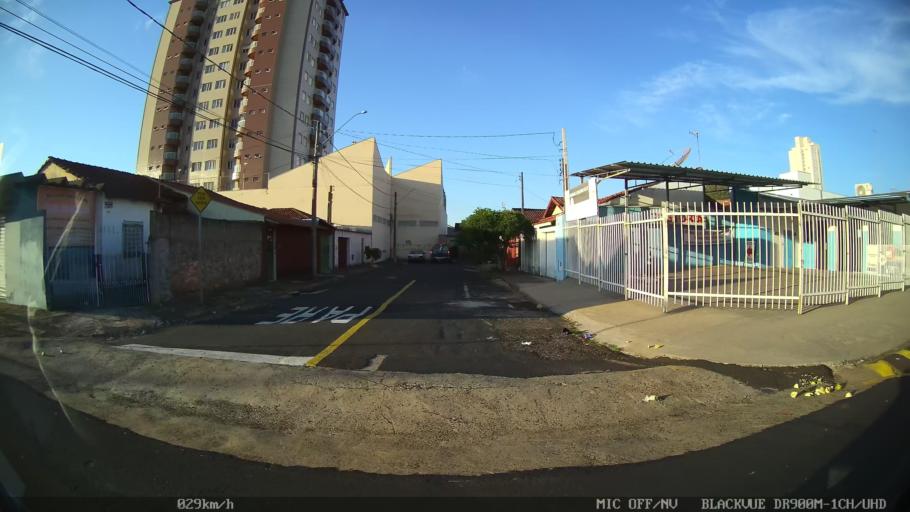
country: BR
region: Sao Paulo
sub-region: Franca
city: Franca
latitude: -20.5255
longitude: -47.3936
